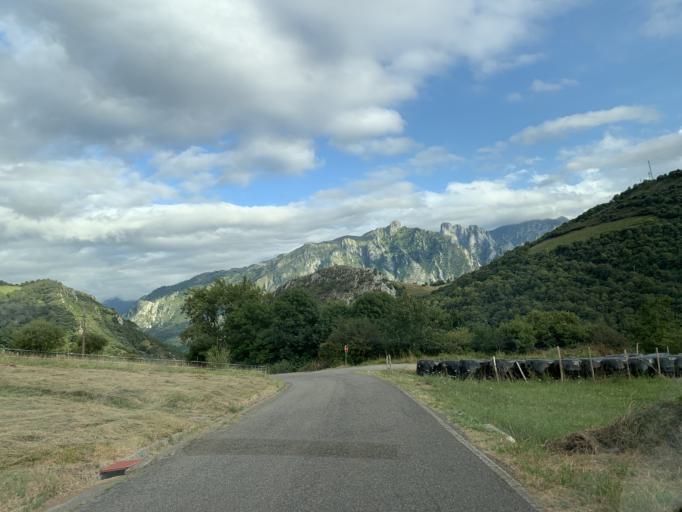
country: ES
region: Asturias
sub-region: Province of Asturias
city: Carrena
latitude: 43.3196
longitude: -4.8539
